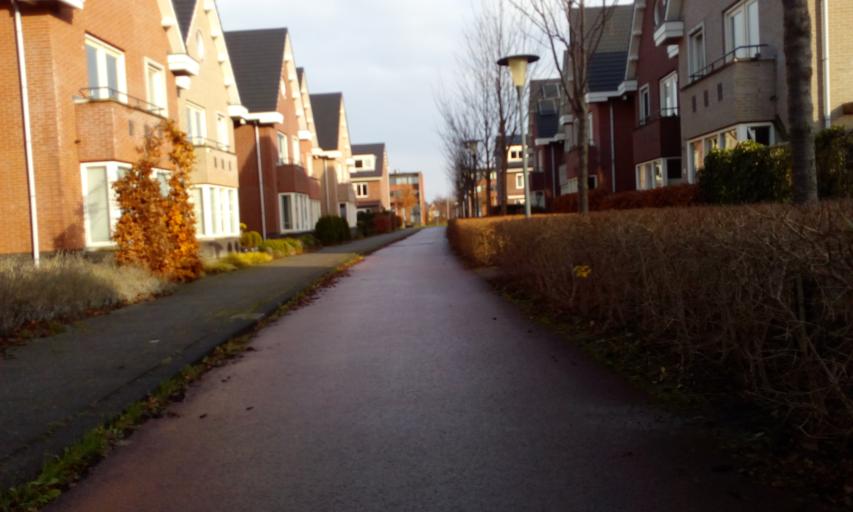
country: NL
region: South Holland
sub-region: Gemeente Rijnwoude
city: Benthuizen
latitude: 52.0557
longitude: 4.5444
